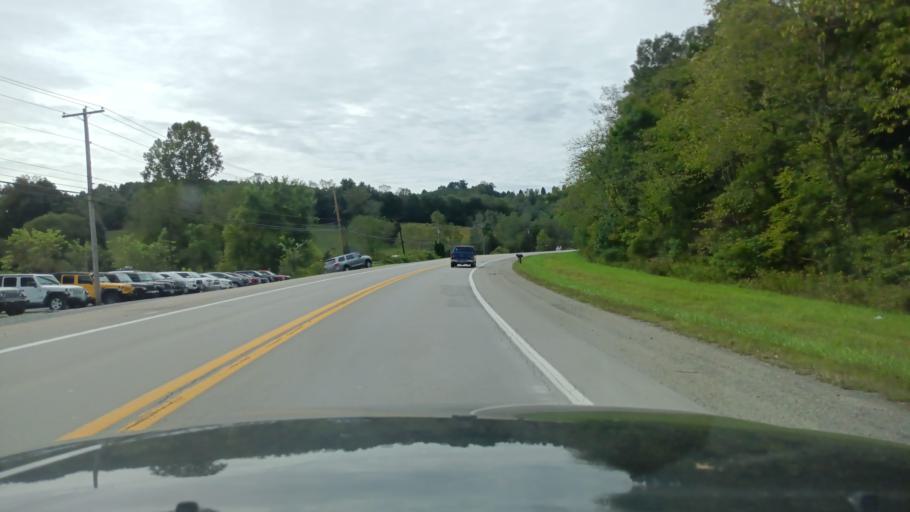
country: US
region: West Virginia
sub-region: Taylor County
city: Grafton
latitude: 39.3382
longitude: -80.0616
